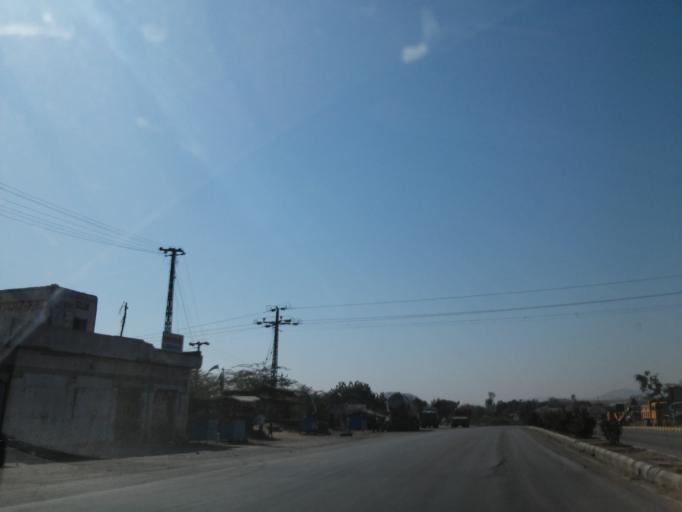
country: IN
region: Rajasthan
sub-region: Dungarpur
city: Dungarpur
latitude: 24.0760
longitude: 73.6840
